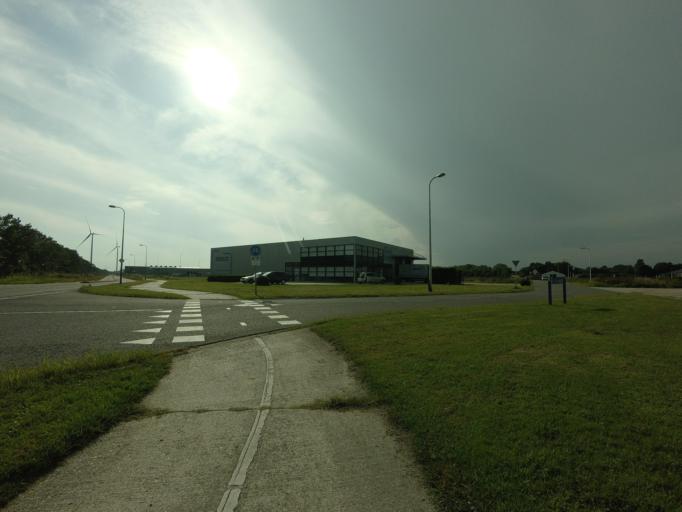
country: NL
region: Drenthe
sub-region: Gemeente Coevorden
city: Coevorden
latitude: 52.6526
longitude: 6.7272
